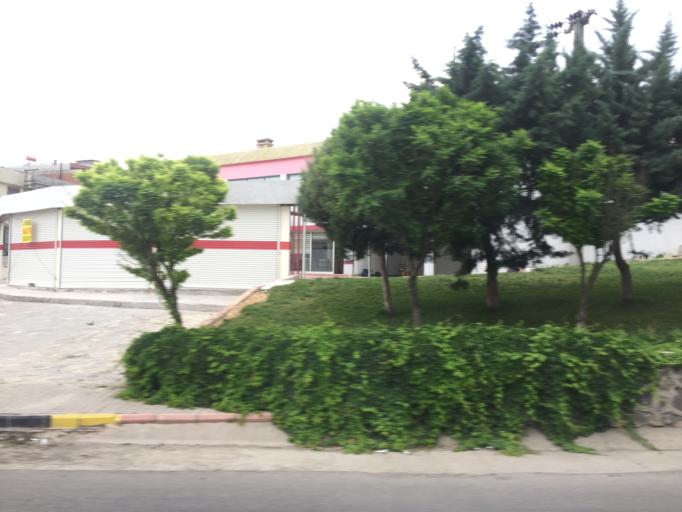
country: TR
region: Gaziantep
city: Gaziantep
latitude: 37.0418
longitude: 37.4242
